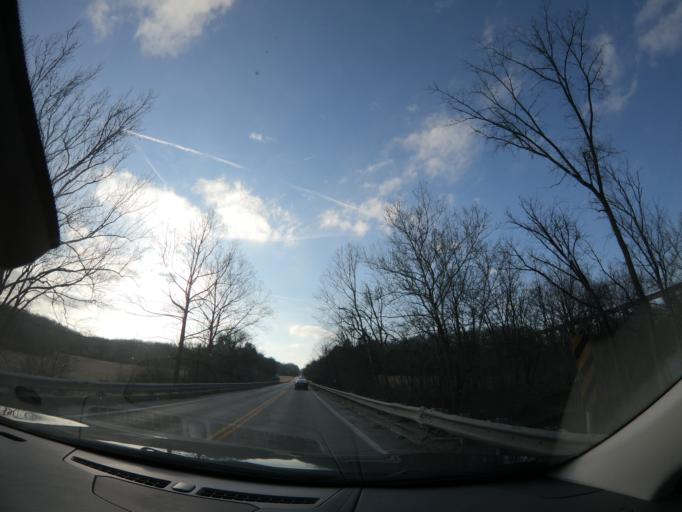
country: US
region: Kentucky
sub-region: Jefferson County
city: Middletown
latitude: 38.1908
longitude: -85.4872
